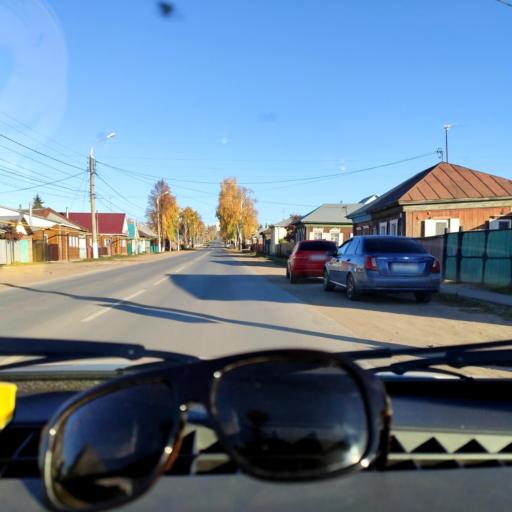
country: RU
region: Bashkortostan
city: Blagoveshchensk
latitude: 55.0365
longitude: 55.9641
